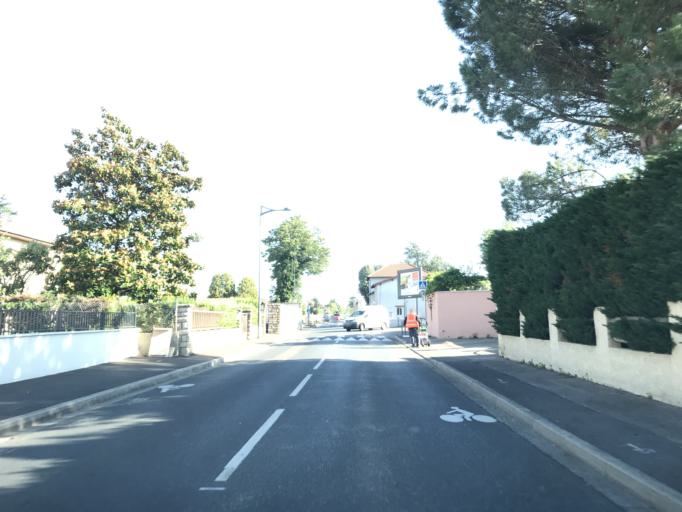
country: FR
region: Rhone-Alpes
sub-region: Departement du Rhone
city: Mions
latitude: 45.6547
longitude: 4.9540
